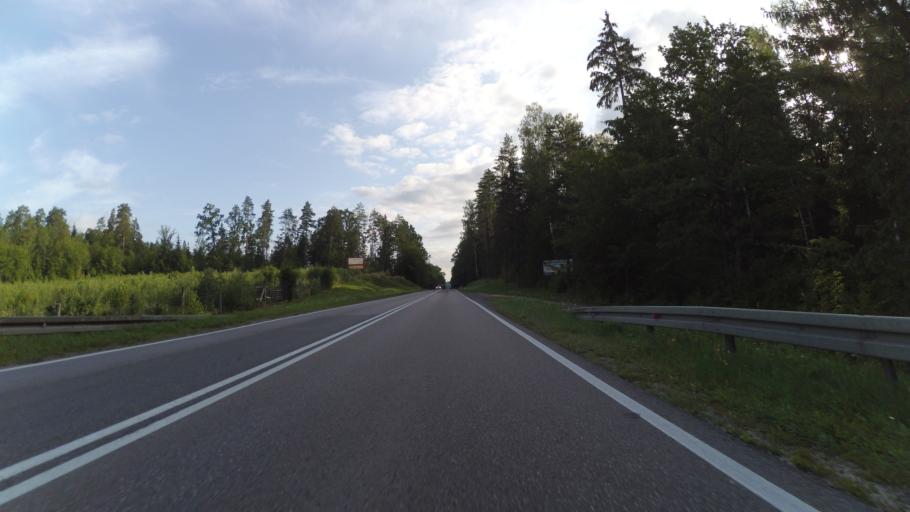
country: PL
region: Podlasie
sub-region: Powiat bialostocki
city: Czarna Bialostocka
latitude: 53.2864
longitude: 23.2846
